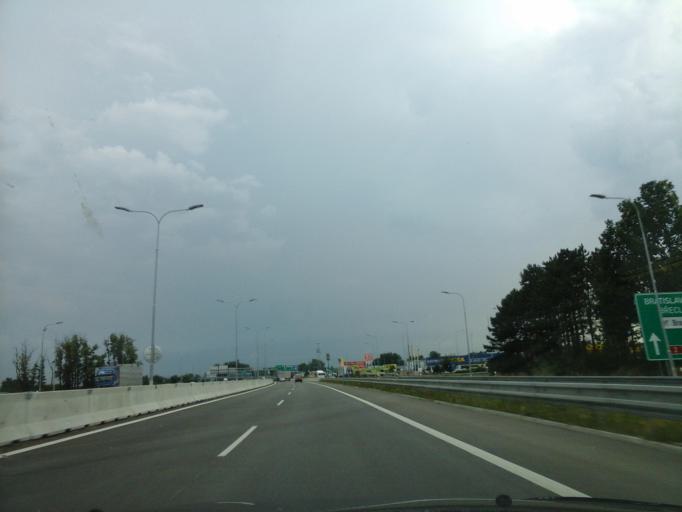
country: CZ
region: South Moravian
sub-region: Mesto Brno
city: Brno
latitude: 49.1580
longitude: 16.6306
